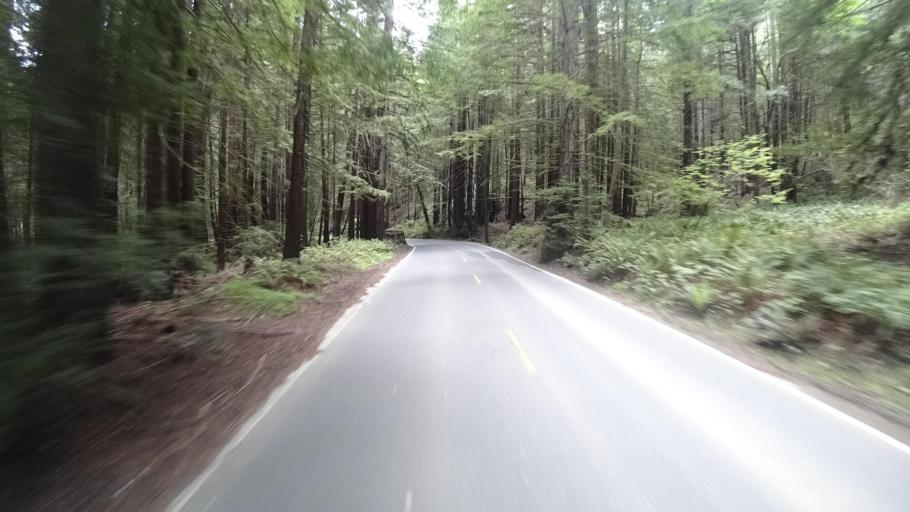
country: US
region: California
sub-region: Humboldt County
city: Redway
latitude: 40.1242
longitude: -123.8457
